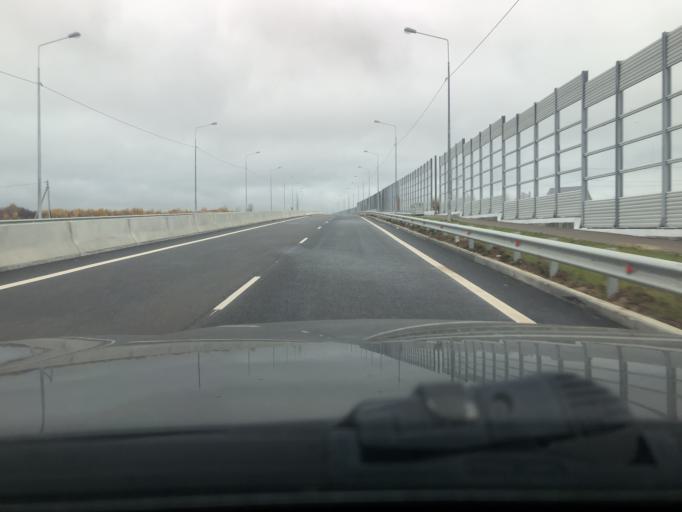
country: RU
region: Moskovskaya
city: Sergiyev Posad
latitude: 56.3100
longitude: 38.0982
